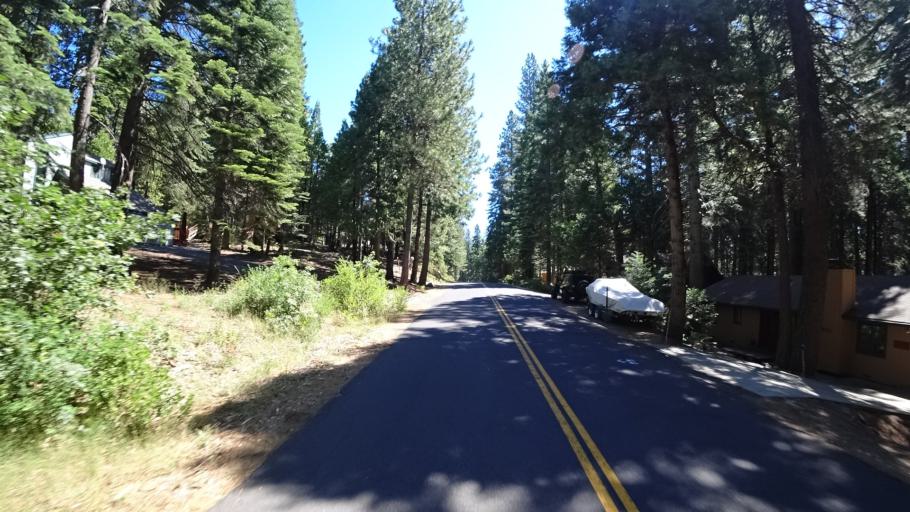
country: US
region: California
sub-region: Calaveras County
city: Arnold
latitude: 38.2956
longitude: -120.2821
